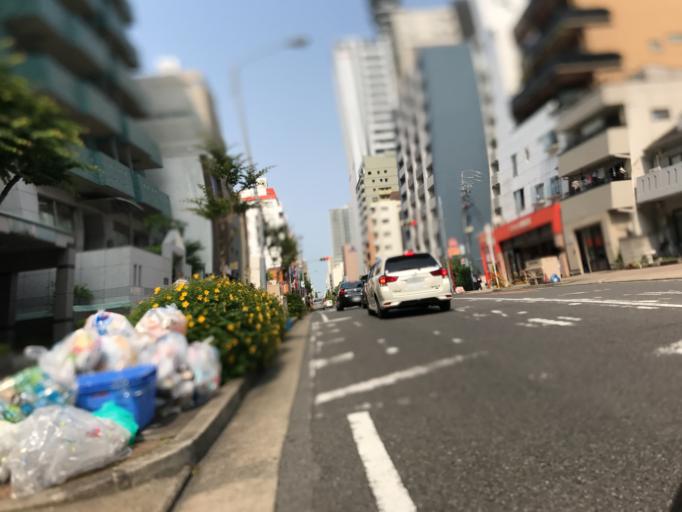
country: JP
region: Aichi
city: Nagoya-shi
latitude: 35.1759
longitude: 136.9120
